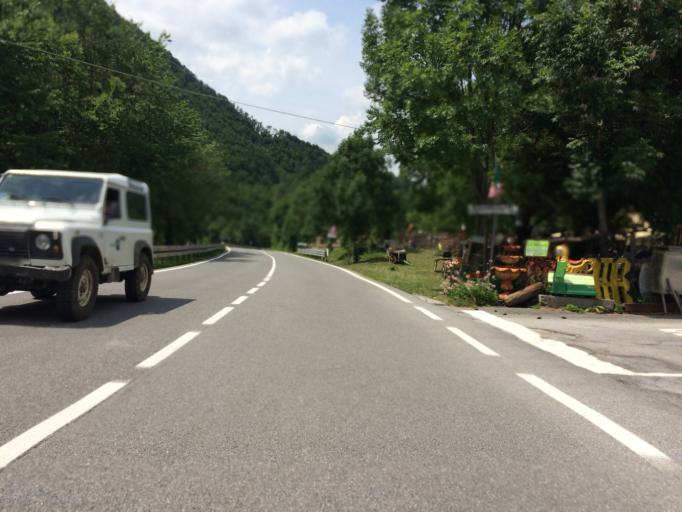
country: IT
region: Piedmont
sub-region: Provincia di Cuneo
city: Limone Piemonte
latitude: 44.2224
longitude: 7.5668
